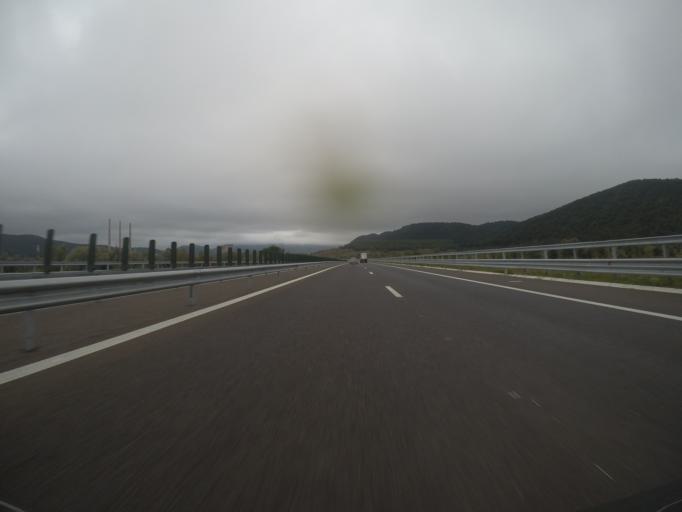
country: RO
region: Hunedoara
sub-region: Comuna Vetel
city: Vetel
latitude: 45.9265
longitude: 22.8356
